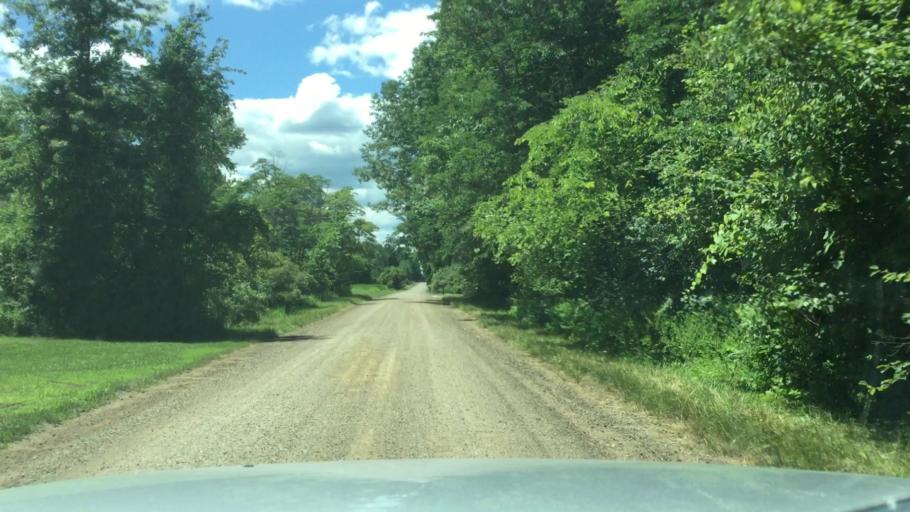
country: US
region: Michigan
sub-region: Saginaw County
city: Saint Charles
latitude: 43.3580
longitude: -84.1742
